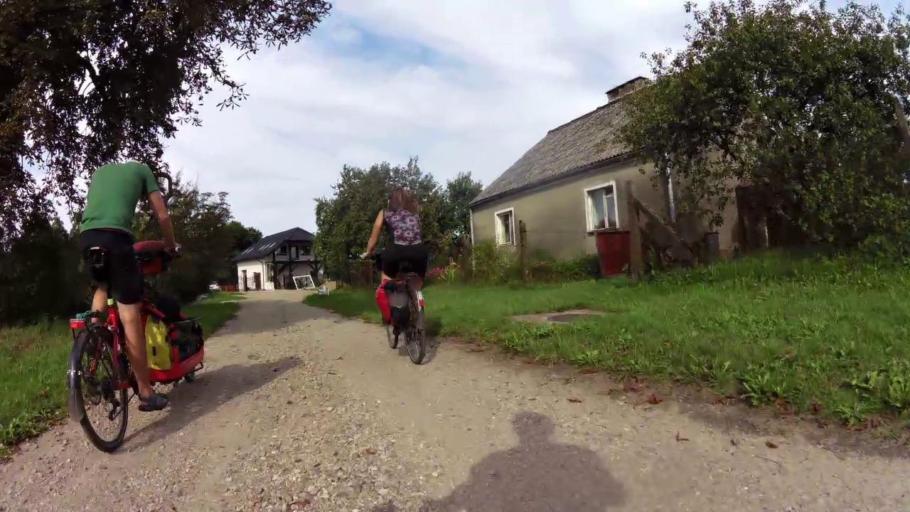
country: PL
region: West Pomeranian Voivodeship
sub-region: Powiat stargardzki
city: Insko
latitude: 53.4449
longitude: 15.6487
